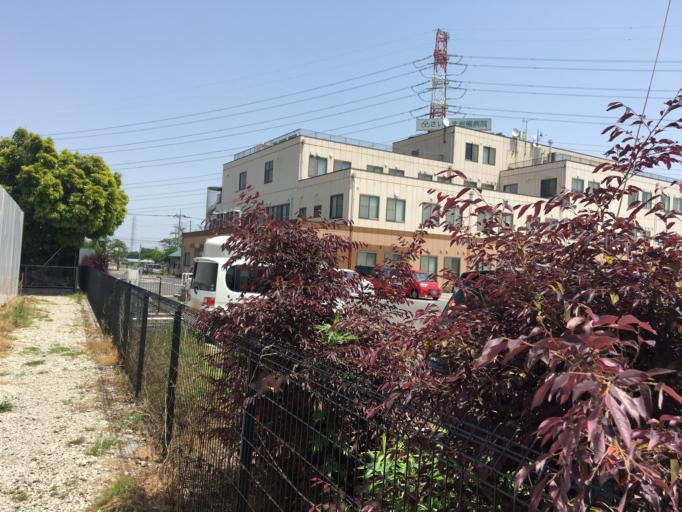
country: JP
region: Saitama
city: Kasukabe
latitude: 35.9775
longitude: 139.7111
